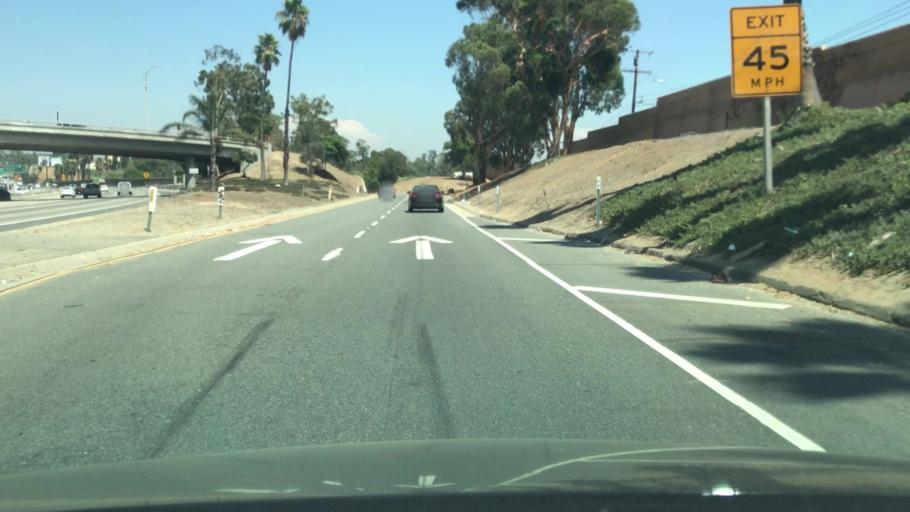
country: US
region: California
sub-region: Los Angeles County
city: East Los Angeles
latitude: 34.0315
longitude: -118.1855
